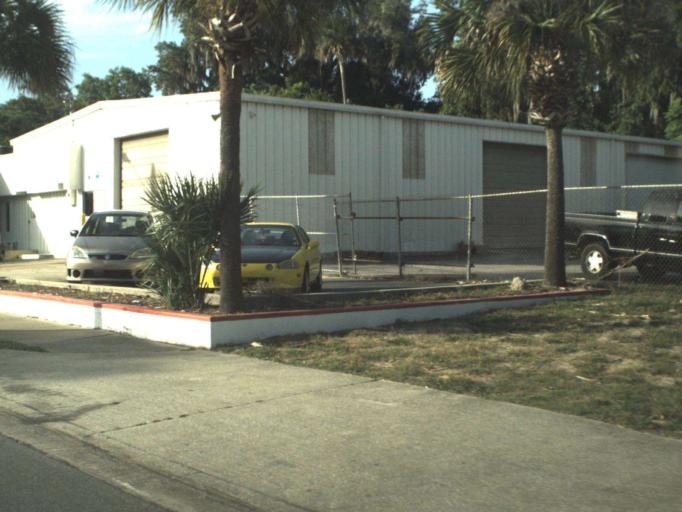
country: US
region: Florida
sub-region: Volusia County
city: New Smyrna Beach
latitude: 29.0388
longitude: -80.9329
